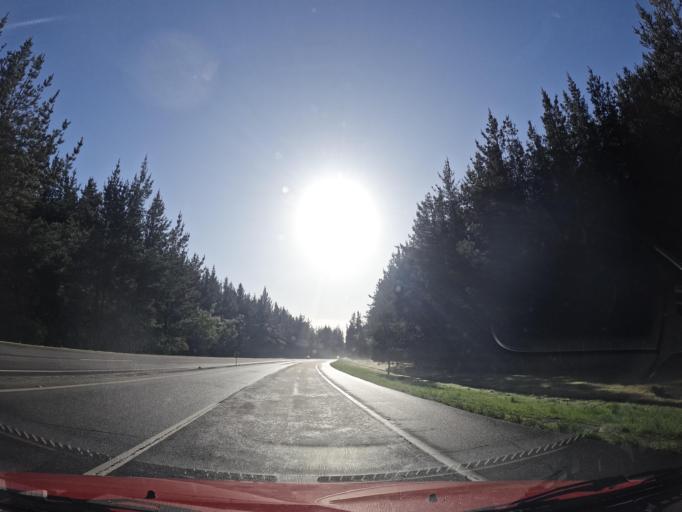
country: CL
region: Biobio
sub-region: Provincia de Concepcion
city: Penco
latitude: -36.7537
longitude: -72.9249
